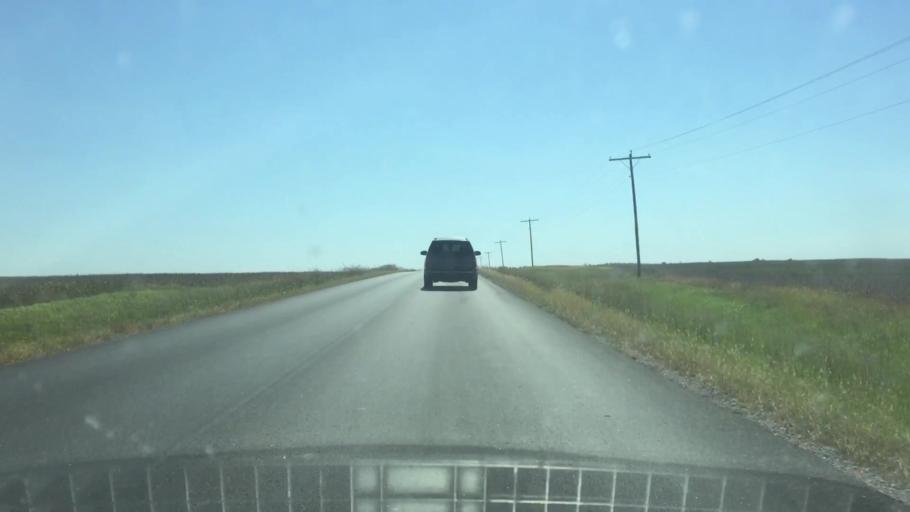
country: US
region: Kansas
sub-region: Marshall County
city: Marysville
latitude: 39.8686
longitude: -96.6016
